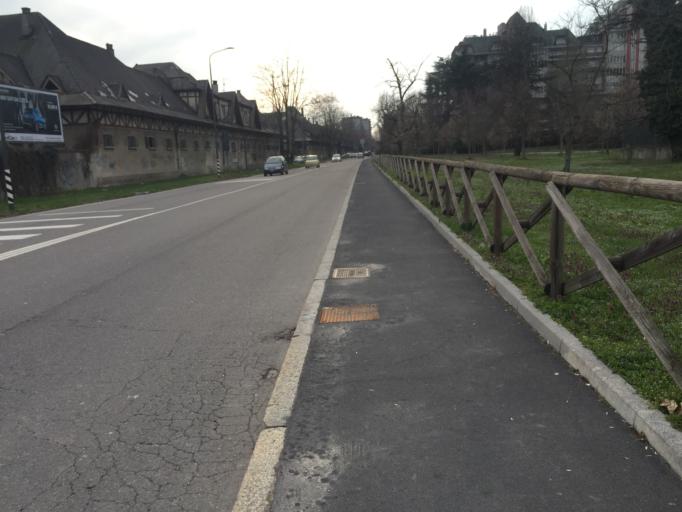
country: IT
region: Lombardy
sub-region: Citta metropolitana di Milano
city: Baranzate
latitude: 45.4860
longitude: 9.1241
